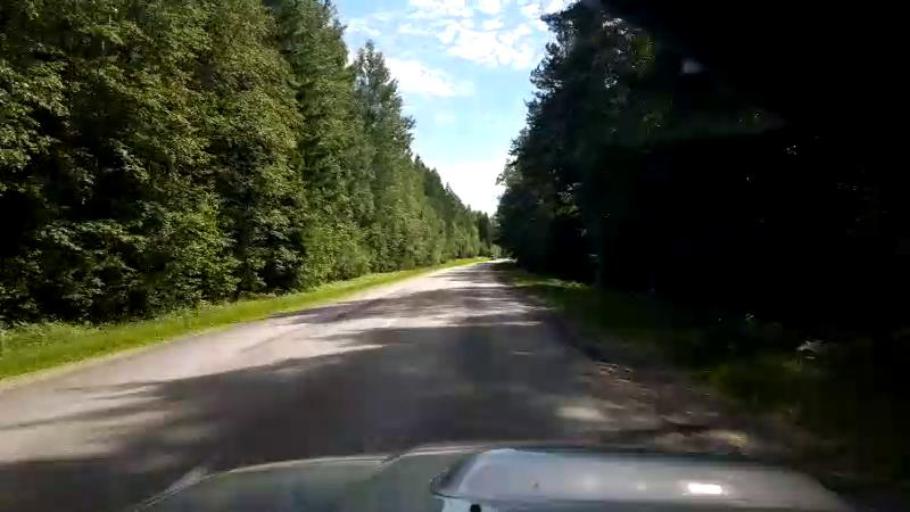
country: EE
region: Laeaene-Virumaa
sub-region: Rakke vald
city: Rakke
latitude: 58.8770
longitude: 26.2956
